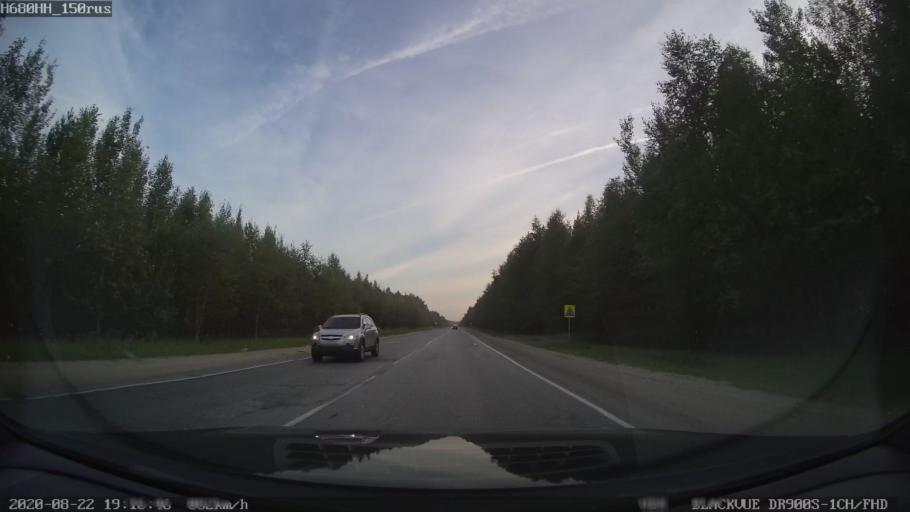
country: RU
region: Tverskaya
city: Sakharovo
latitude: 56.9516
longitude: 36.0145
